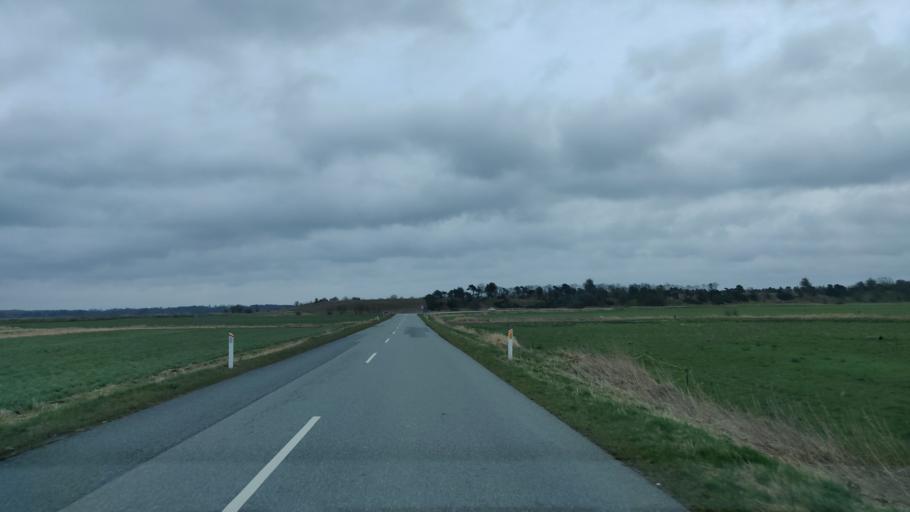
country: DK
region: Central Jutland
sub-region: Skive Kommune
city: Hojslev
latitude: 56.5702
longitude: 9.2419
